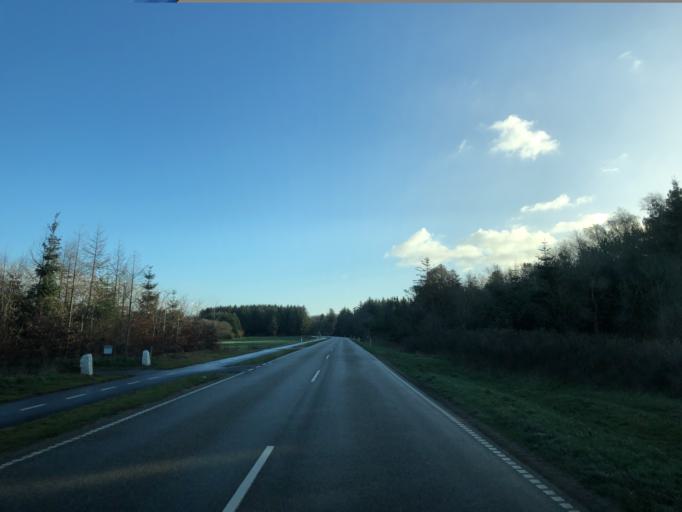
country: DK
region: Central Jutland
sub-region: Holstebro Kommune
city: Ulfborg
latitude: 56.1977
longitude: 8.2827
